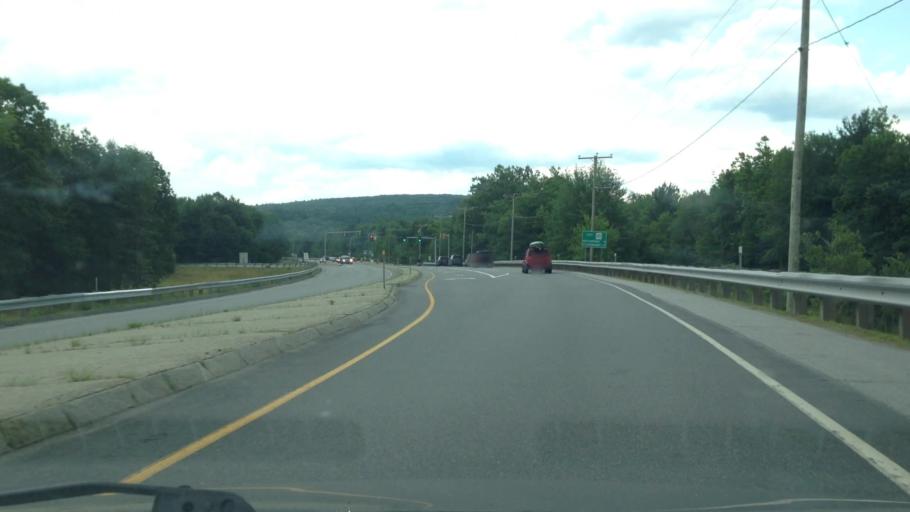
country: US
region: New Hampshire
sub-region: Cheshire County
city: Keene
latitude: 42.9162
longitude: -72.2653
